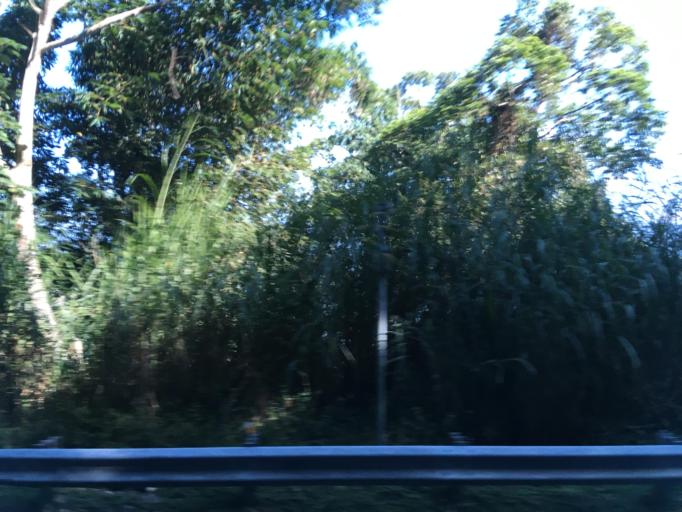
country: TW
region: Taiwan
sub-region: Chiayi
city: Jiayi Shi
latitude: 23.4341
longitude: 120.6633
